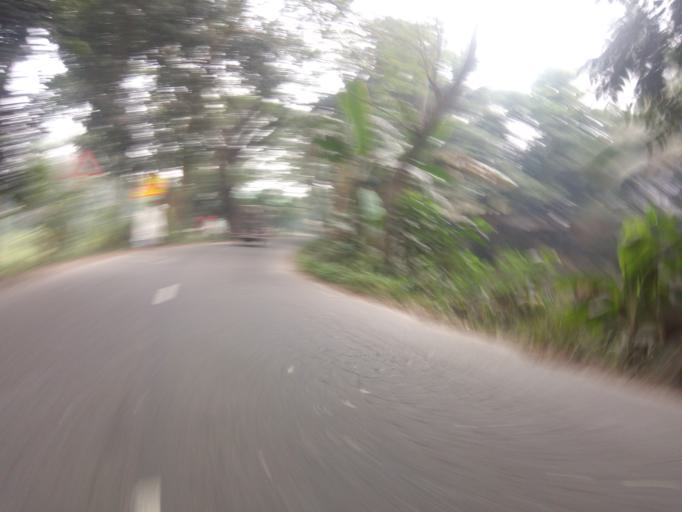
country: BD
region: Dhaka
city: Narayanganj
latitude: 23.5357
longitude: 90.4858
